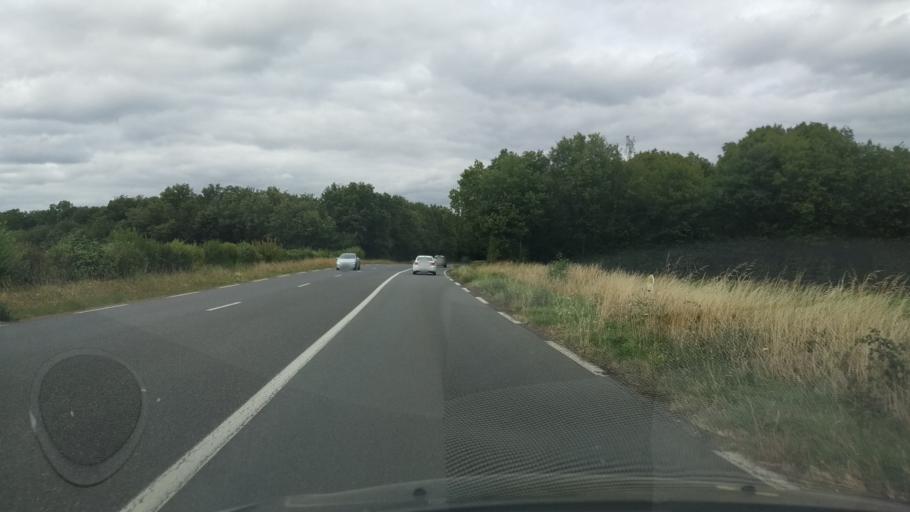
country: FR
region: Poitou-Charentes
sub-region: Departement de la Vienne
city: Smarves
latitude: 46.5240
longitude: 0.3543
